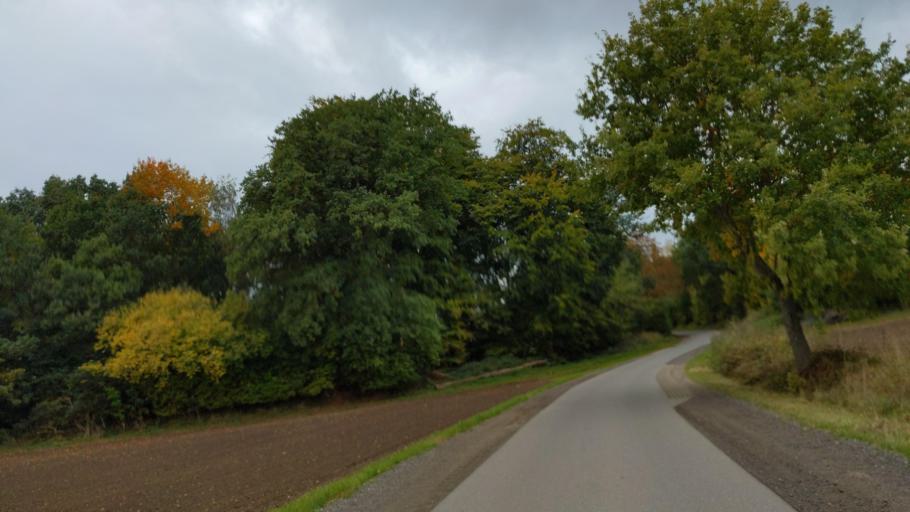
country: DE
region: Schleswig-Holstein
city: Neustadt in Holstein
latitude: 54.1382
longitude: 10.7967
